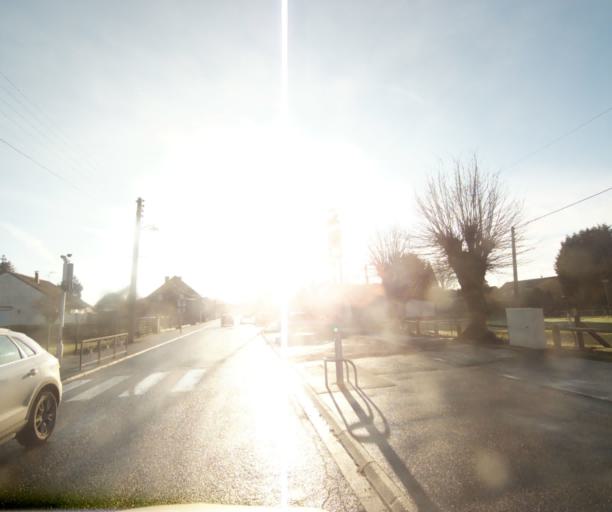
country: FR
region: Nord-Pas-de-Calais
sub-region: Departement du Nord
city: Onnaing
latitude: 50.3948
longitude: 3.5926
